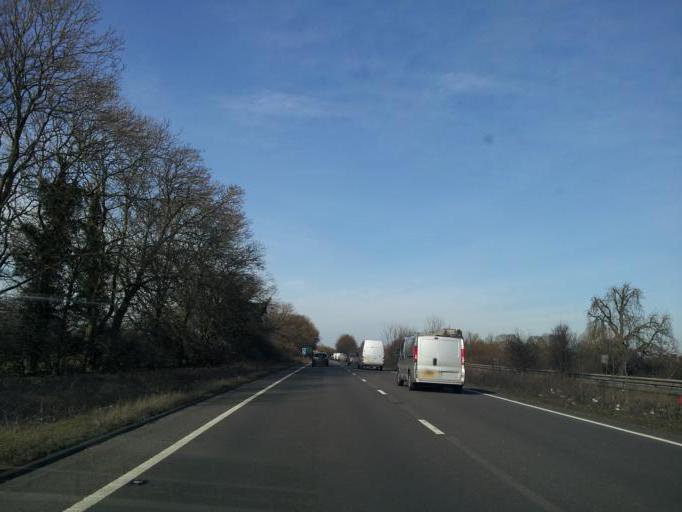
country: GB
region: England
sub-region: District of Rutland
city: Greetham
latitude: 52.7287
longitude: -0.5983
